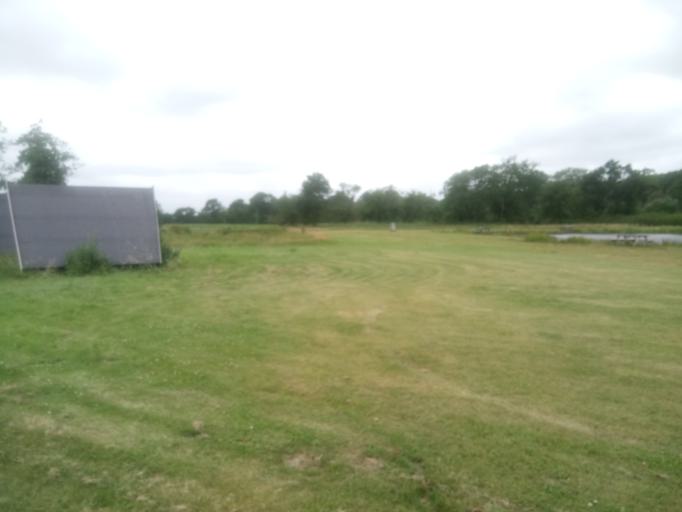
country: DK
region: Central Jutland
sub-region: Herning Kommune
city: Kibaek
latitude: 55.9538
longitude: 8.7241
